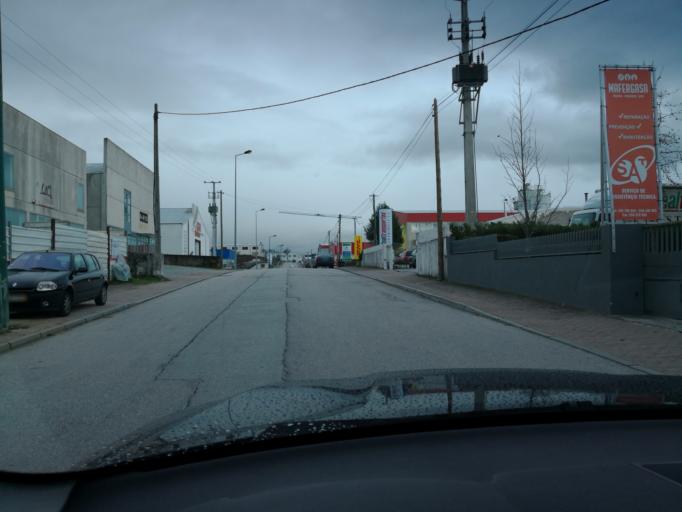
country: PT
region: Vila Real
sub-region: Vila Real
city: Vila Real
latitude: 41.2797
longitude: -7.7092
